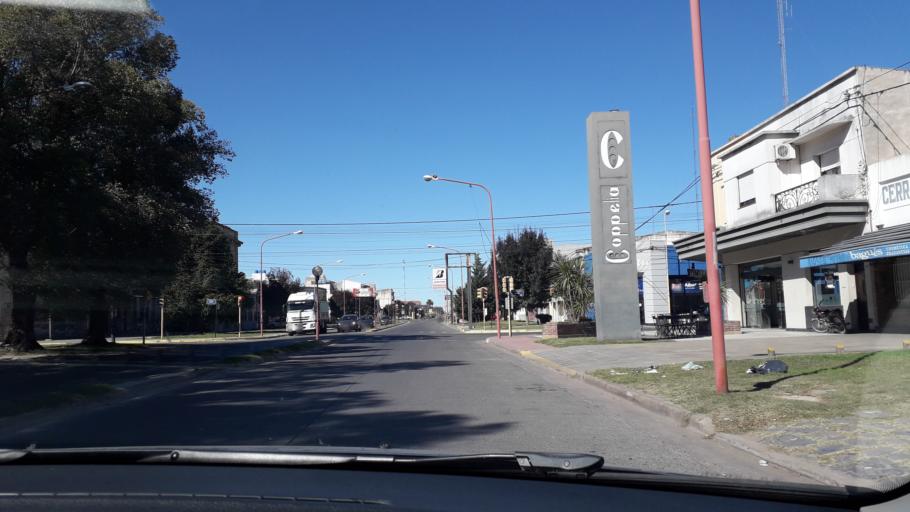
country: AR
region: Buenos Aires
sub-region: Partido de Azul
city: Azul
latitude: -36.7803
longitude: -59.8555
